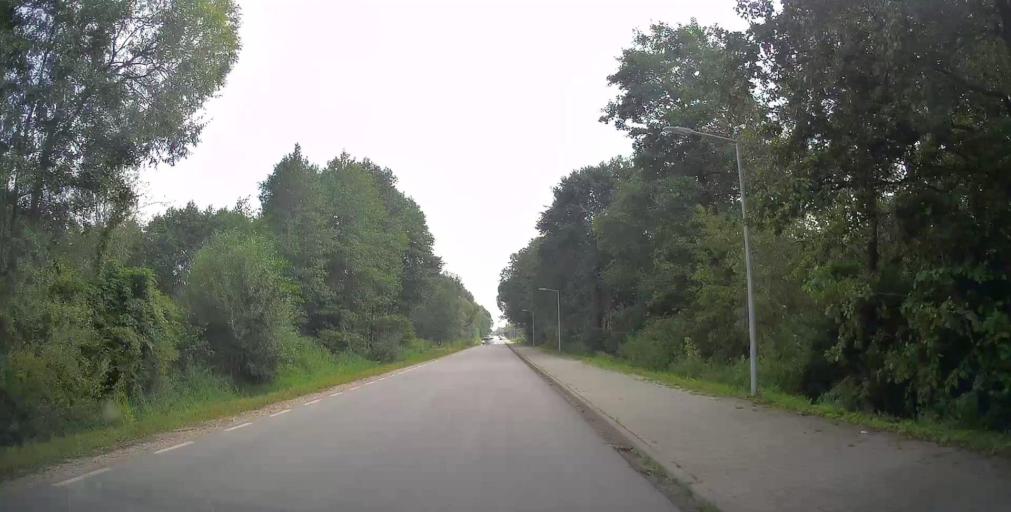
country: PL
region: Masovian Voivodeship
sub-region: Powiat bialobrzeski
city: Sucha
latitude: 51.6143
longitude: 20.9637
